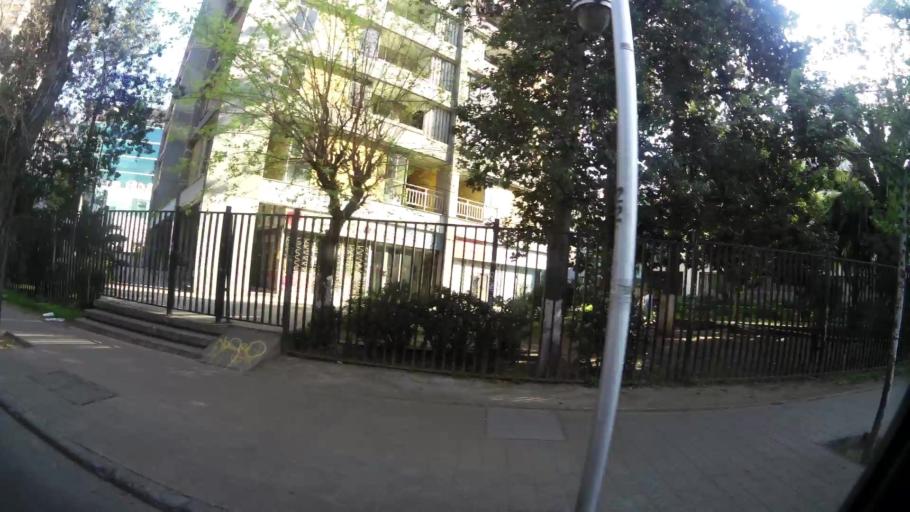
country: CL
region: Santiago Metropolitan
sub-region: Provincia de Santiago
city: Santiago
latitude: -33.4431
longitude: -70.6397
